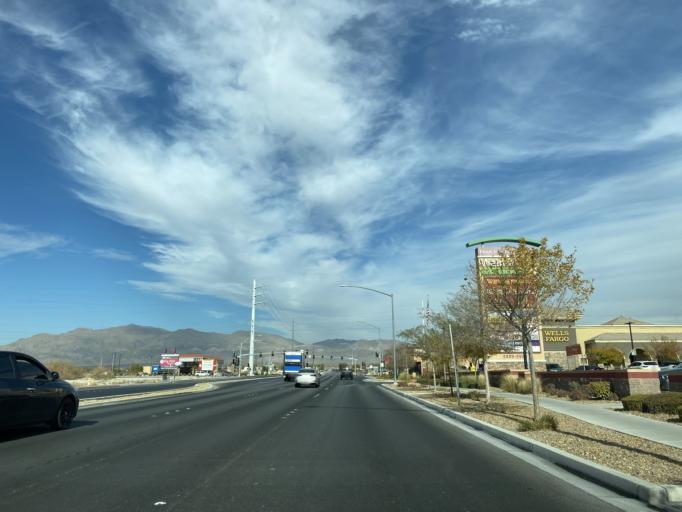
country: US
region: Nevada
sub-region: Clark County
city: Nellis Air Force Base
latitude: 36.2672
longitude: -115.1169
